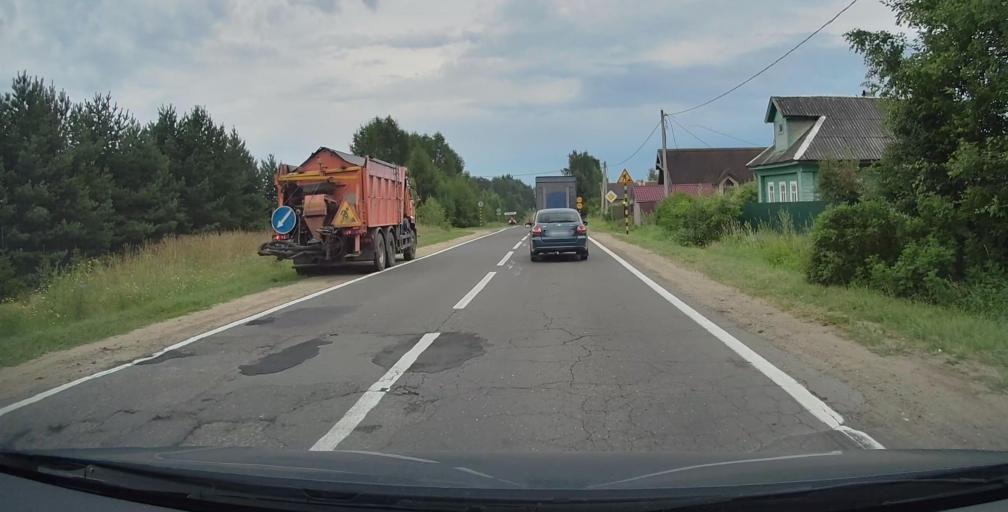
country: RU
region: Jaroslavl
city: Myshkin
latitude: 57.8577
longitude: 38.5089
